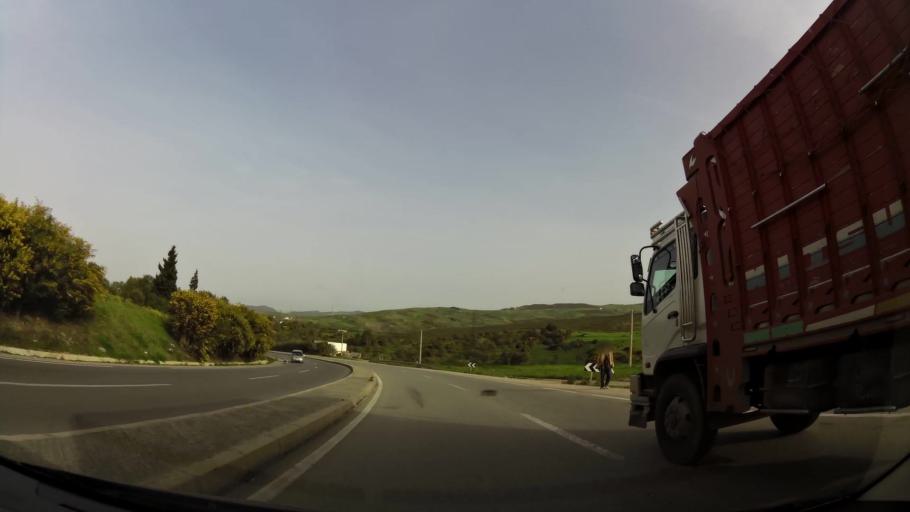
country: MA
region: Tanger-Tetouan
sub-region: Tetouan
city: Saddina
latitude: 35.5489
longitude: -5.5420
